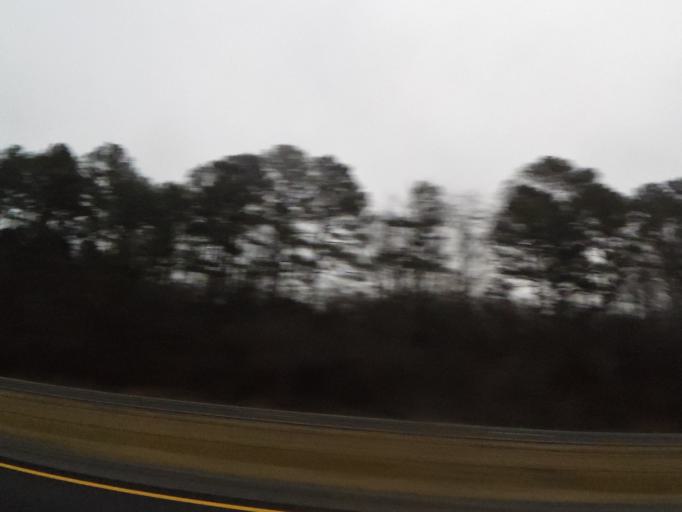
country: US
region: Alabama
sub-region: Cullman County
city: Cullman
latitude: 34.2229
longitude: -86.8760
